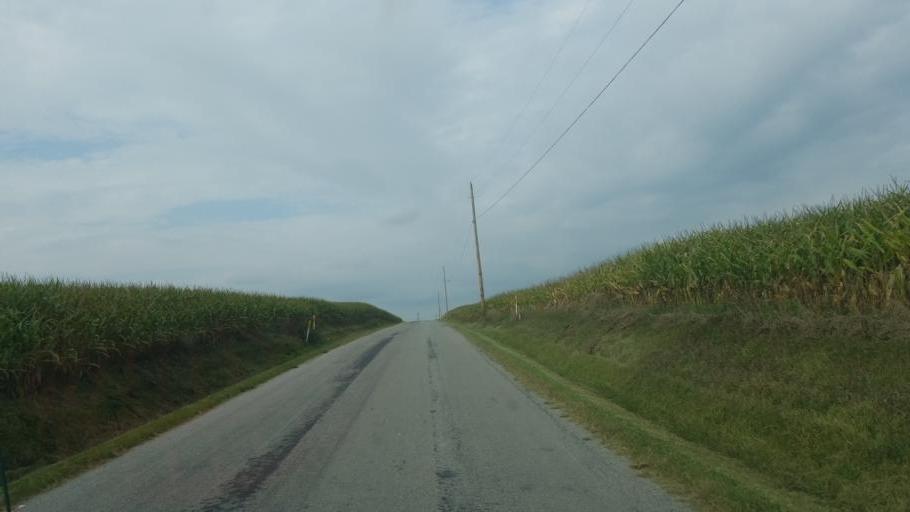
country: US
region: Ohio
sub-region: Wayne County
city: West Salem
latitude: 40.9715
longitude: -82.0539
